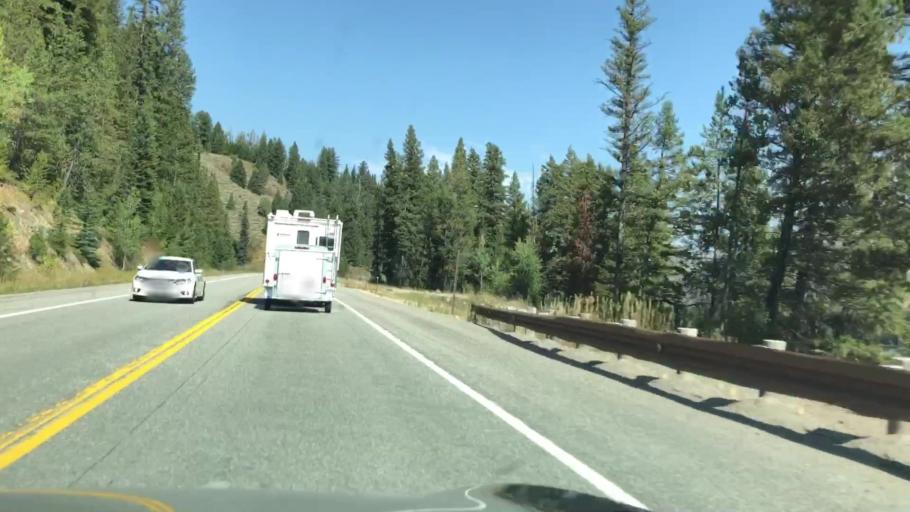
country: US
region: Wyoming
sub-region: Teton County
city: Hoback
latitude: 43.2468
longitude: -110.7769
